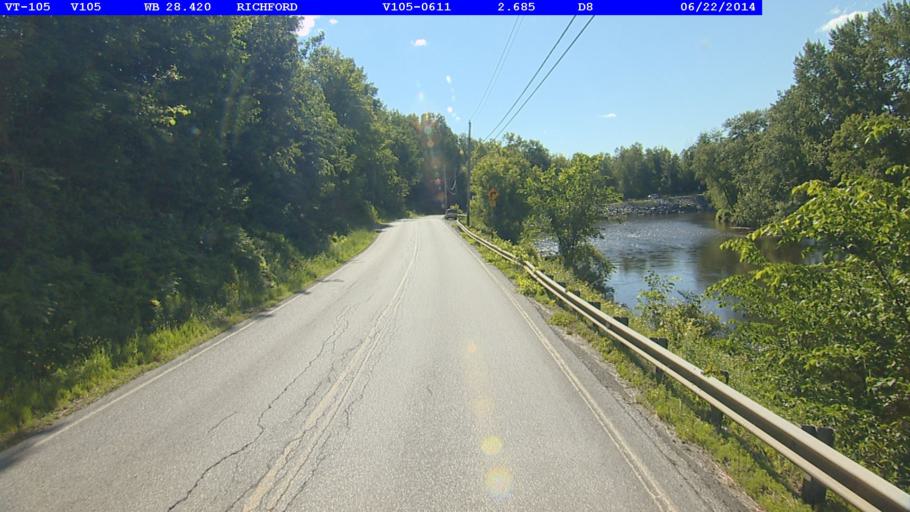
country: US
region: Vermont
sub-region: Franklin County
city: Richford
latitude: 44.9850
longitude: -72.6643
